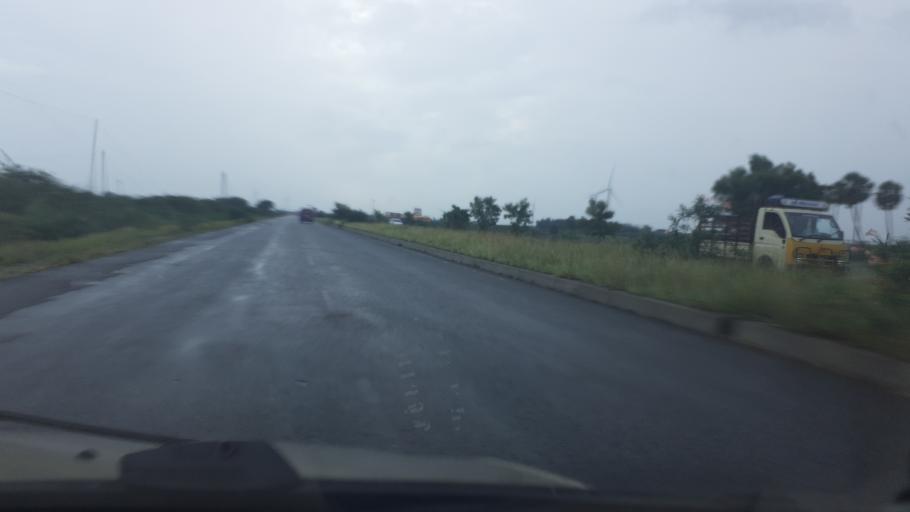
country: IN
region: Tamil Nadu
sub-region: Thoothukkudi
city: Kayattar
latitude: 9.0053
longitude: 77.7817
